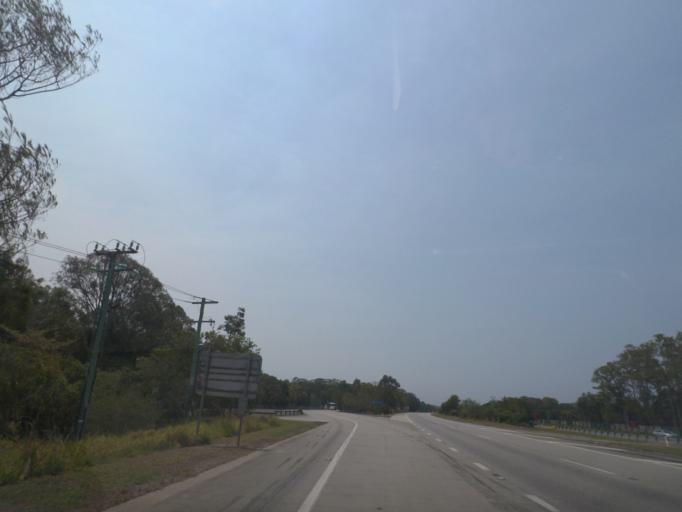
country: AU
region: New South Wales
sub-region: Byron Shire
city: Brunswick Heads
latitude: -28.5993
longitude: 153.5449
